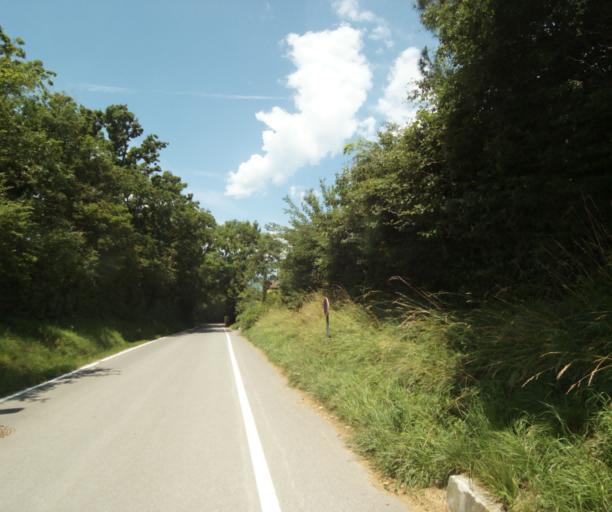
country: FR
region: Rhone-Alpes
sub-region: Departement de la Haute-Savoie
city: Messery
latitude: 46.3654
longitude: 6.3313
